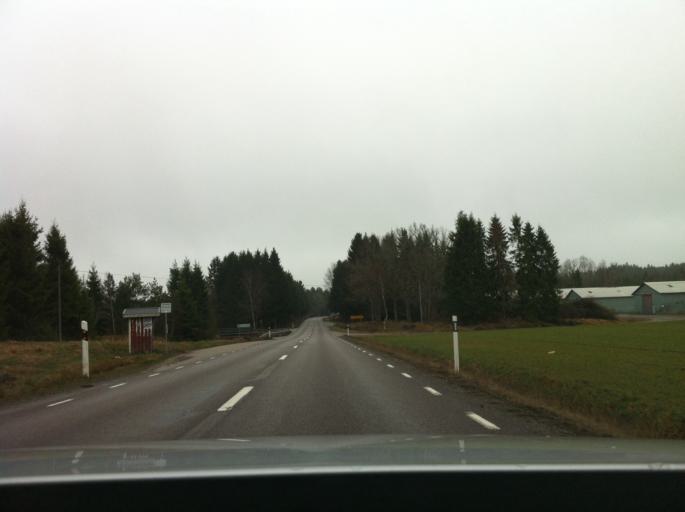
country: SE
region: Vaestra Goetaland
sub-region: Vanersborgs Kommun
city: Vargon
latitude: 58.2170
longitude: 12.4286
